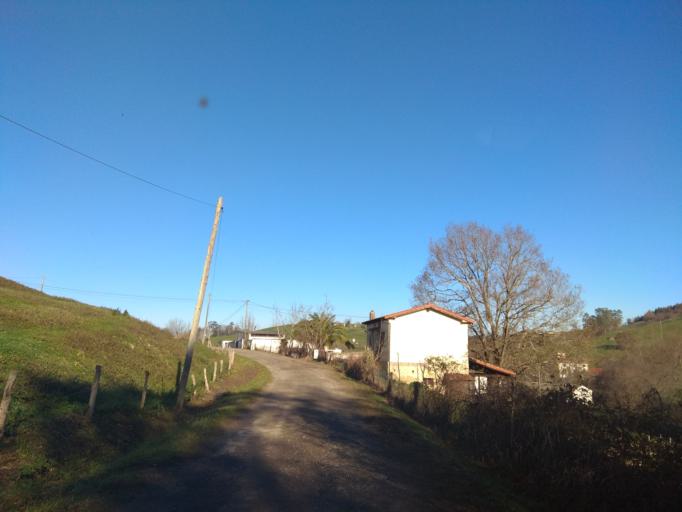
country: ES
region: Cantabria
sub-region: Provincia de Cantabria
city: Entrambasaguas
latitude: 43.3676
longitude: -3.6612
